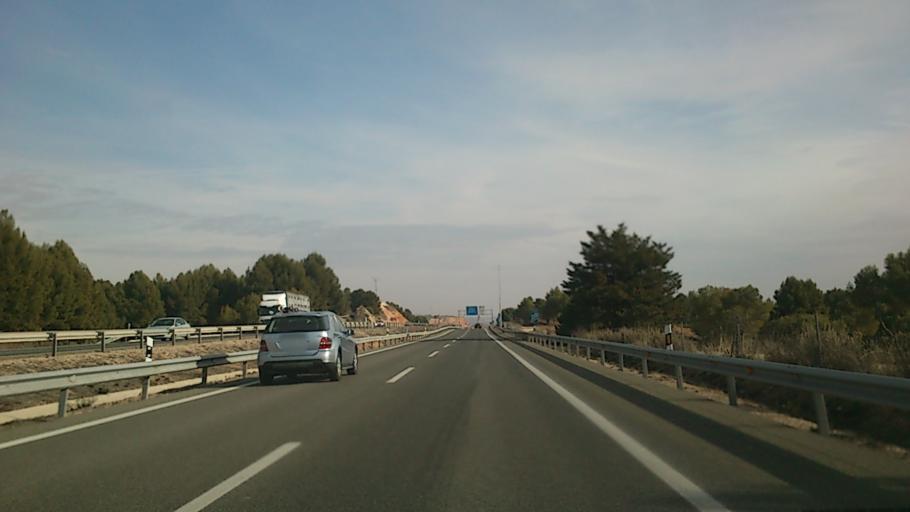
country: ES
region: Aragon
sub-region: Provincia de Zaragoza
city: Monreal de Ariza
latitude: 41.3100
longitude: -2.0875
